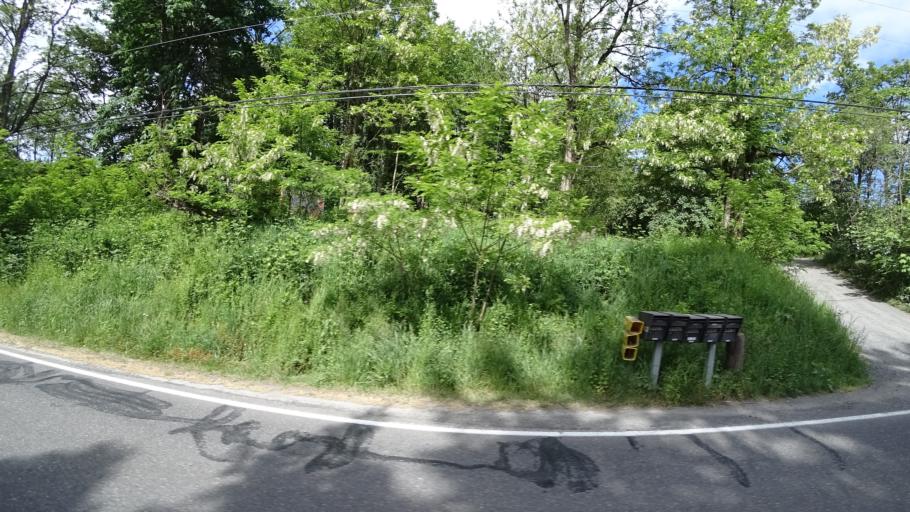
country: US
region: Oregon
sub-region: Washington County
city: Bethany
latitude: 45.6064
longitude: -122.8341
